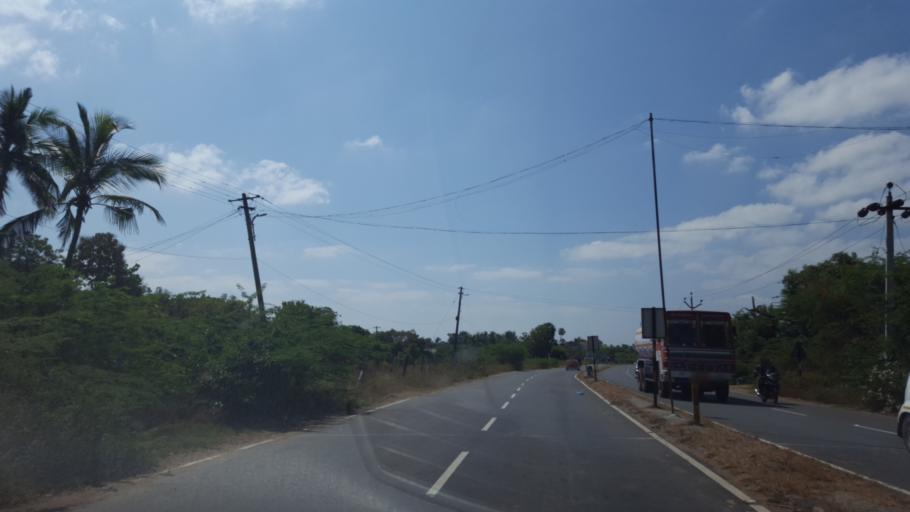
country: IN
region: Tamil Nadu
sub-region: Kancheepuram
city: Mamallapuram
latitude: 12.6458
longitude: 80.1745
